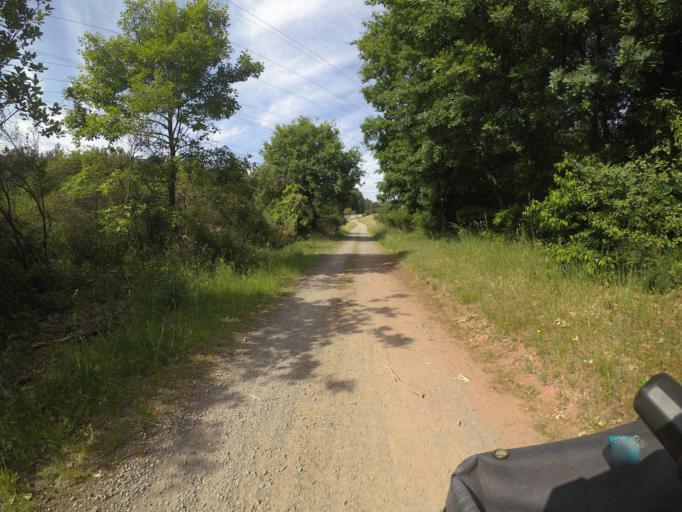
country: DE
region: Rheinland-Pfalz
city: Mackenbach
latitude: 49.4682
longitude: 7.5988
